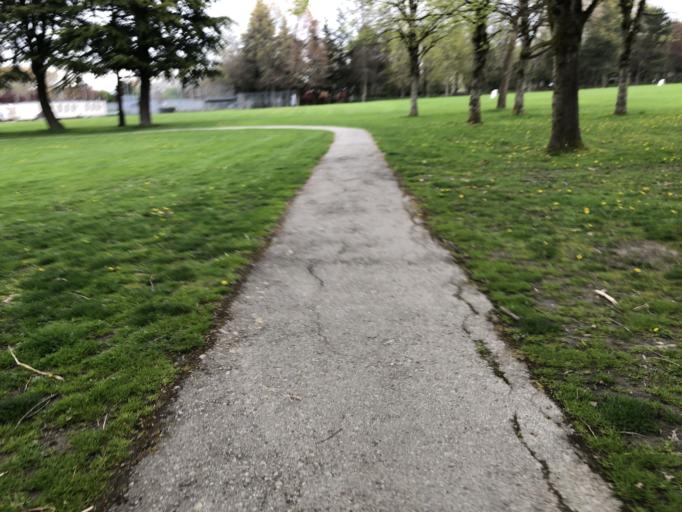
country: CA
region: British Columbia
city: Richmond
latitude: 49.1387
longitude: -123.1275
